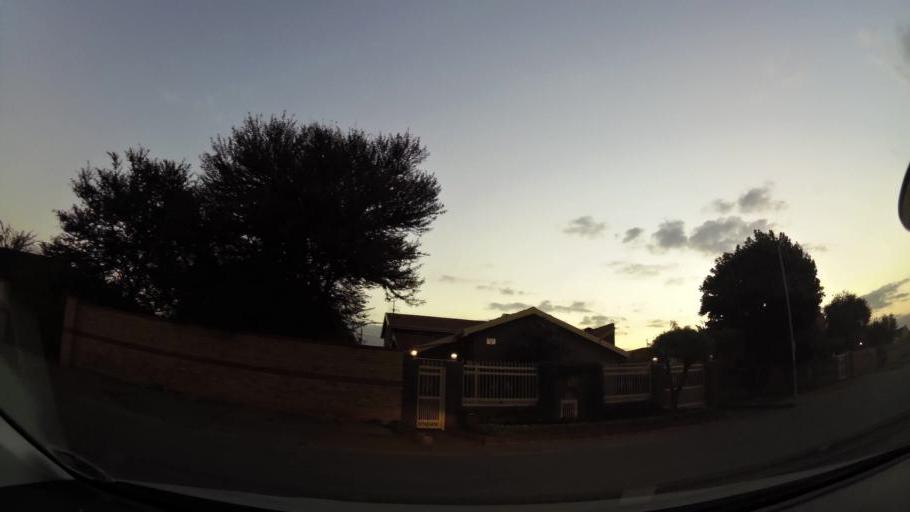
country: ZA
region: Gauteng
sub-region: City of Johannesburg Metropolitan Municipality
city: Soweto
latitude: -26.2731
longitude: 27.9042
